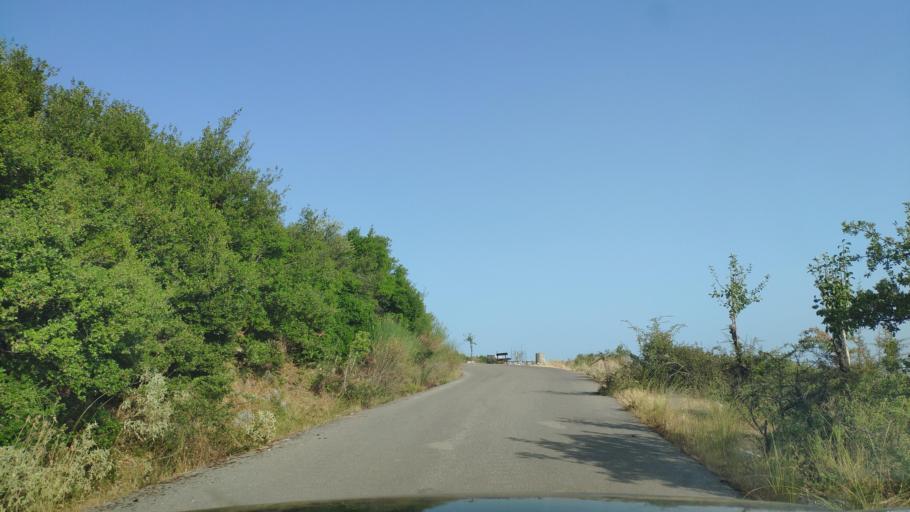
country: GR
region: West Greece
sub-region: Nomos Aitolias kai Akarnanias
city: Monastirakion
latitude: 38.8475
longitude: 20.9757
